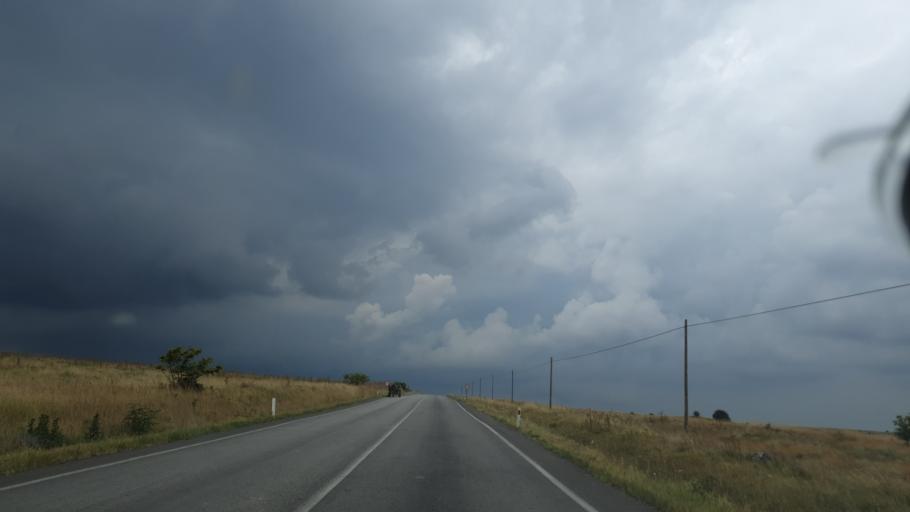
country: TR
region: Tekirdag
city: Hayrabolu
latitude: 41.2188
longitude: 27.0571
